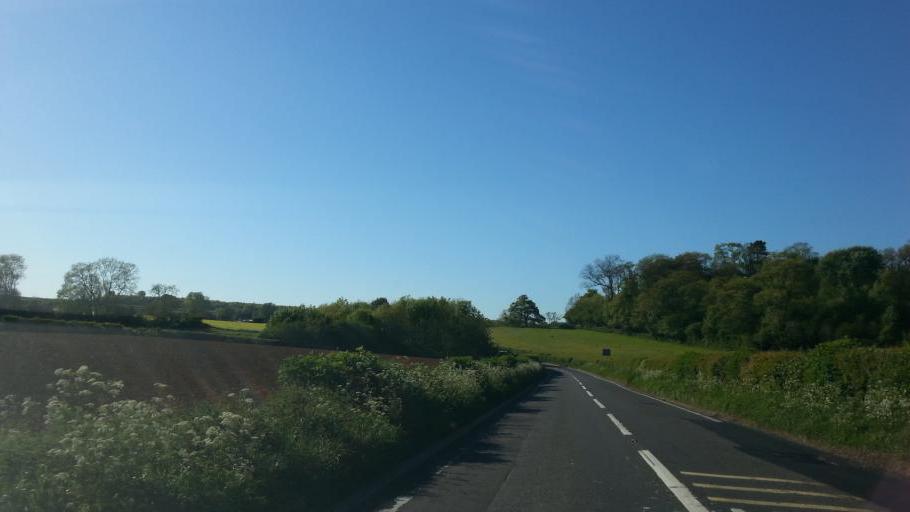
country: GB
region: England
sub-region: Somerset
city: Castle Cary
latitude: 51.0659
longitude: -2.4820
